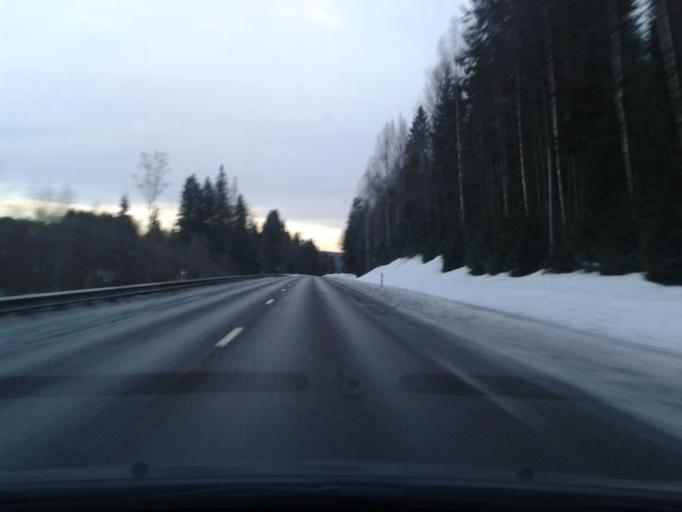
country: SE
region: Vaesternorrland
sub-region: Kramfors Kommun
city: Bollstabruk
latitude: 63.0950
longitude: 17.5253
